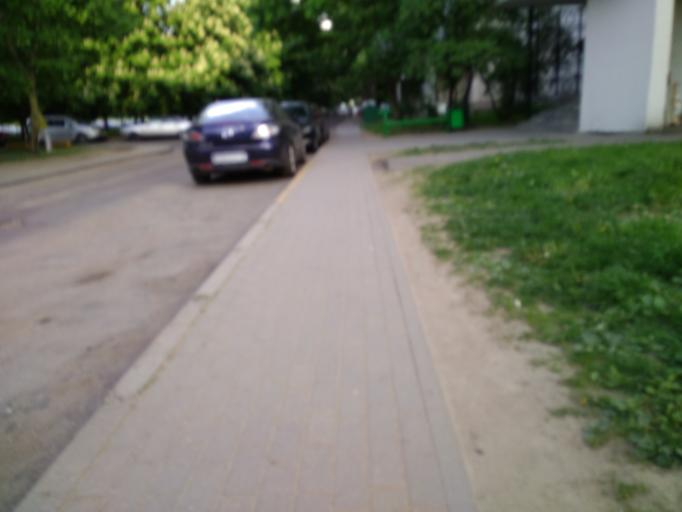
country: BY
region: Minsk
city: Minsk
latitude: 53.9109
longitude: 27.5338
